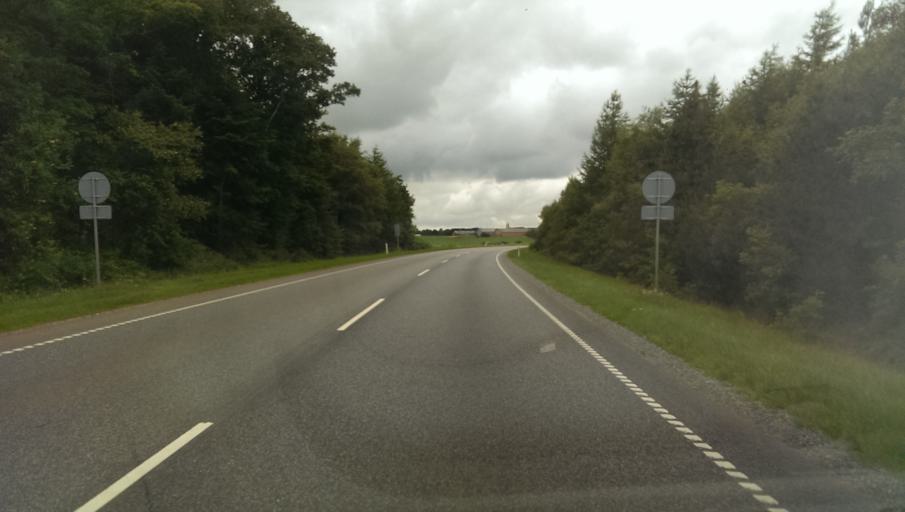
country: DK
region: South Denmark
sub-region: Esbjerg Kommune
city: Bramming
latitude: 55.4806
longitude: 8.6475
